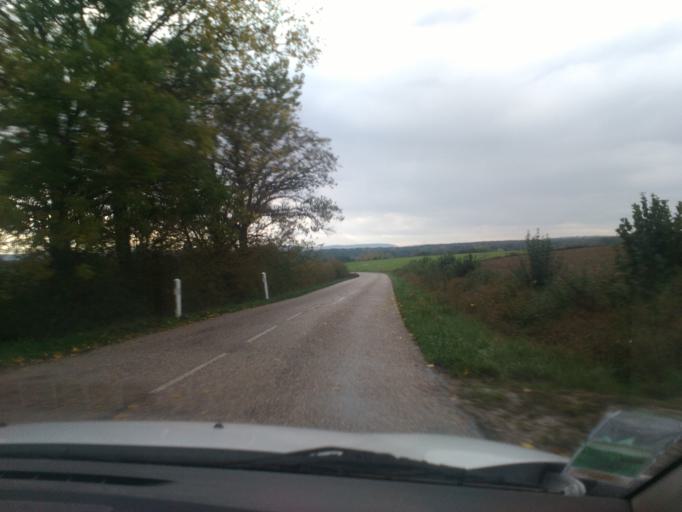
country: FR
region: Lorraine
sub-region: Departement des Vosges
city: Dogneville
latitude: 48.2766
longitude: 6.4851
